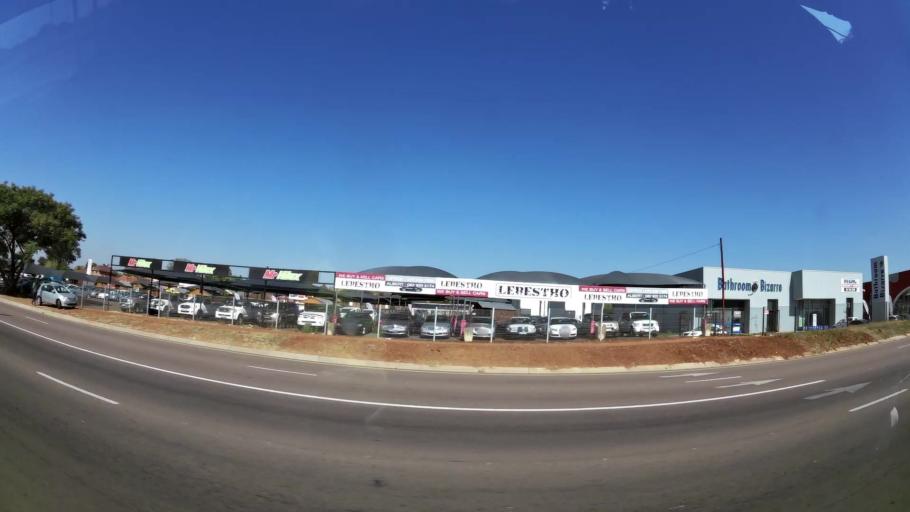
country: ZA
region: Gauteng
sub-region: City of Tshwane Metropolitan Municipality
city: Pretoria
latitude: -25.6838
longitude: 28.2776
